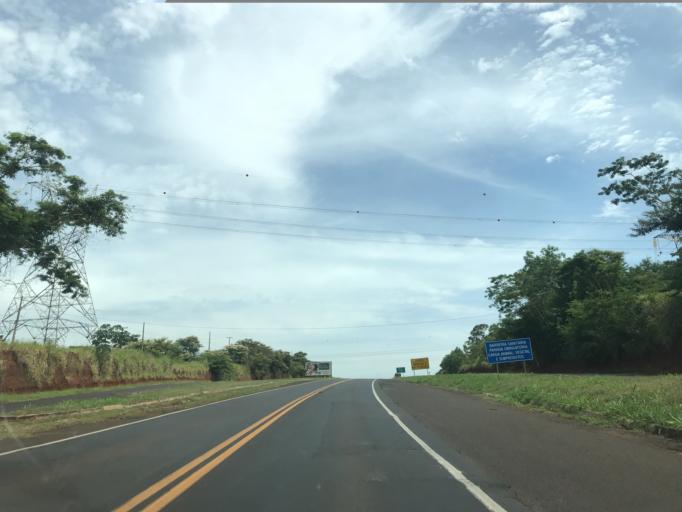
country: BR
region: Sao Paulo
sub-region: Nova Granada
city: Nova Granada
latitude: -20.3019
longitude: -49.2068
